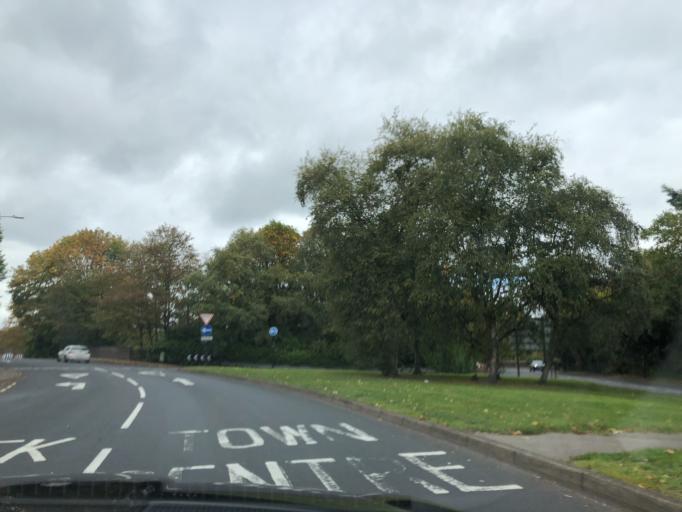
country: GB
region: England
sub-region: Warwickshire
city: Kenilworth
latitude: 52.3354
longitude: -1.5707
